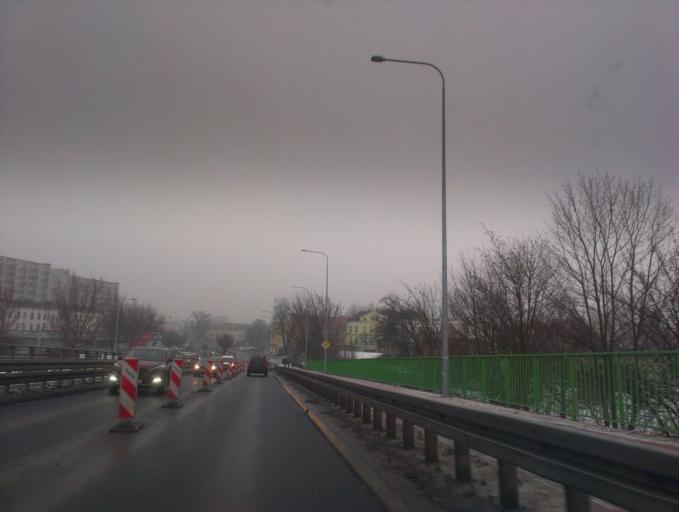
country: PL
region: Greater Poland Voivodeship
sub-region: Powiat pilski
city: Pila
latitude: 53.1439
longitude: 16.7400
